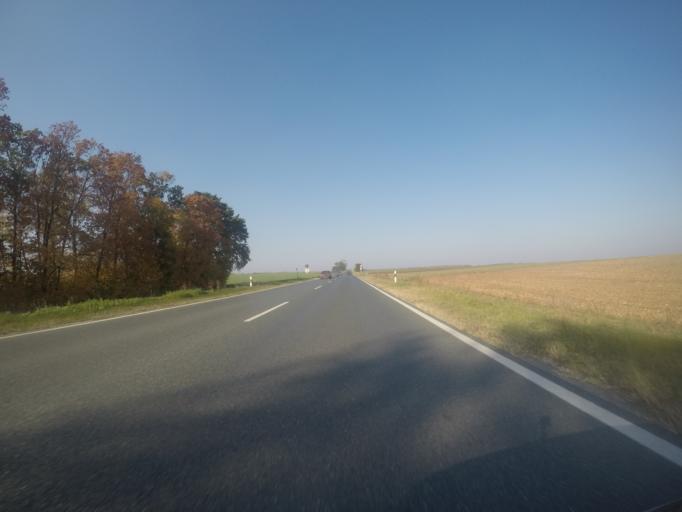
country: HU
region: Tolna
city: Madocsa
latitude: 46.7121
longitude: 18.8872
